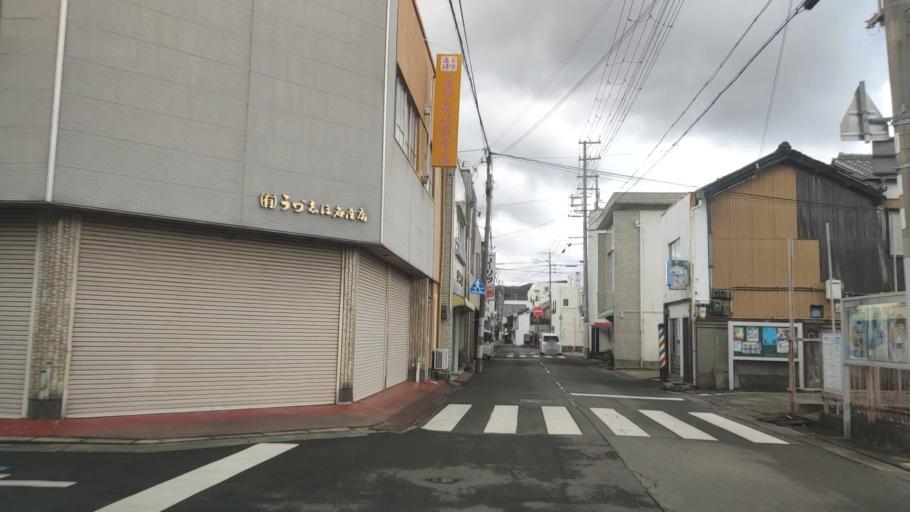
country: JP
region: Hyogo
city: Sumoto
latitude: 34.3430
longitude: 134.8984
